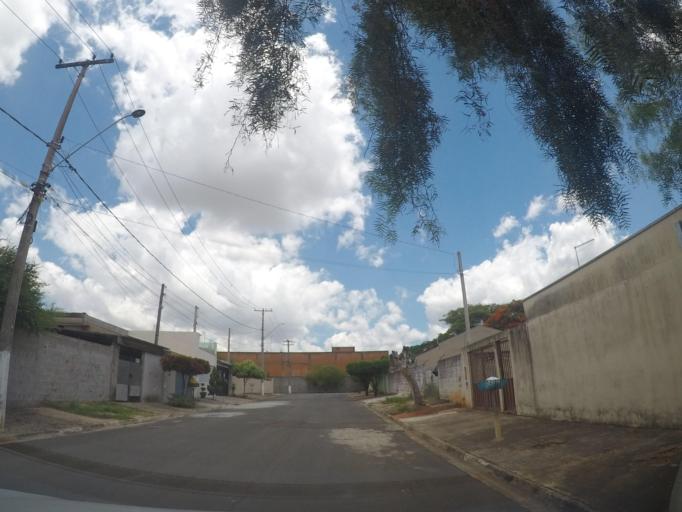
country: BR
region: Sao Paulo
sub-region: Hortolandia
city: Hortolandia
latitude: -22.8182
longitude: -47.2037
